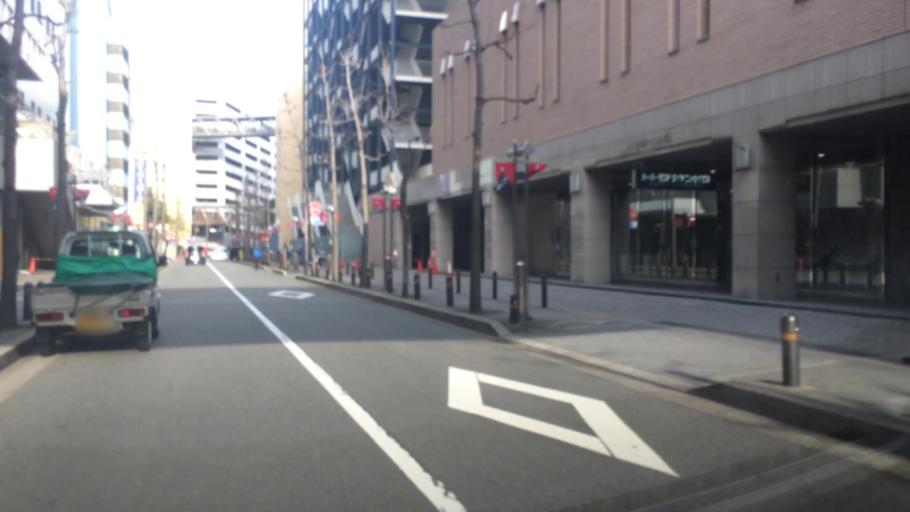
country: JP
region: Hyogo
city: Kobe
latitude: 34.6795
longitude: 135.1812
